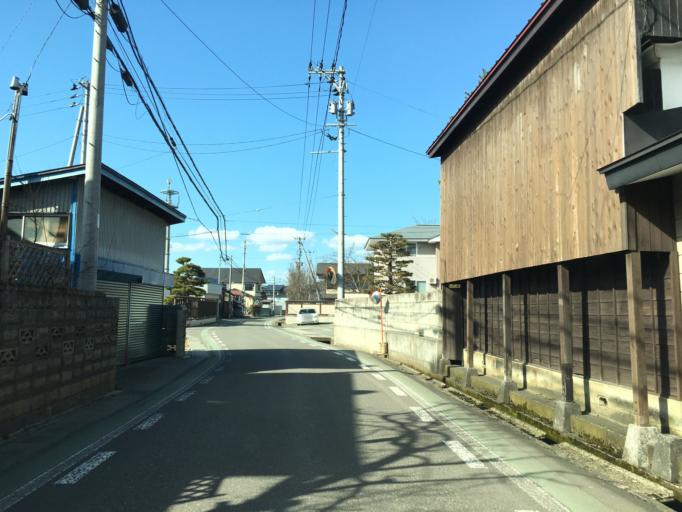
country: JP
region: Yamagata
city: Yonezawa
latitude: 37.9269
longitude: 140.1438
